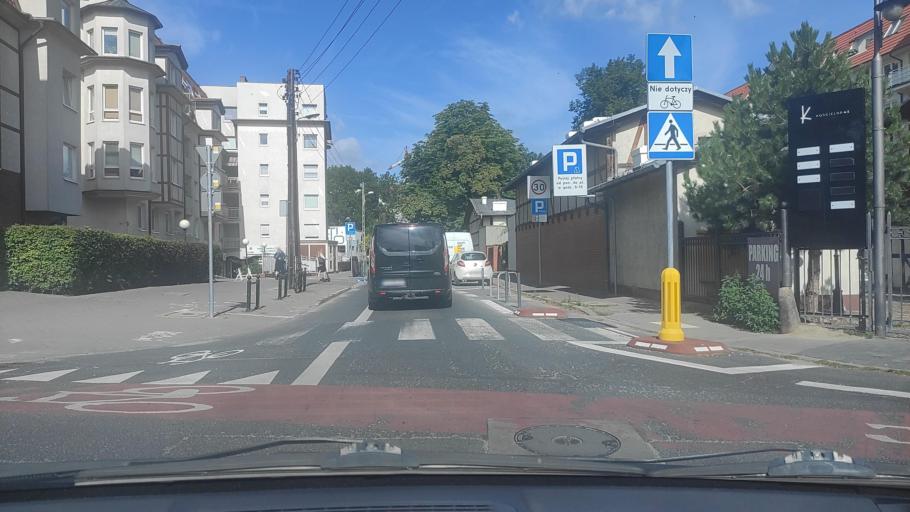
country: PL
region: Greater Poland Voivodeship
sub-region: Poznan
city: Poznan
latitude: 52.4171
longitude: 16.9063
